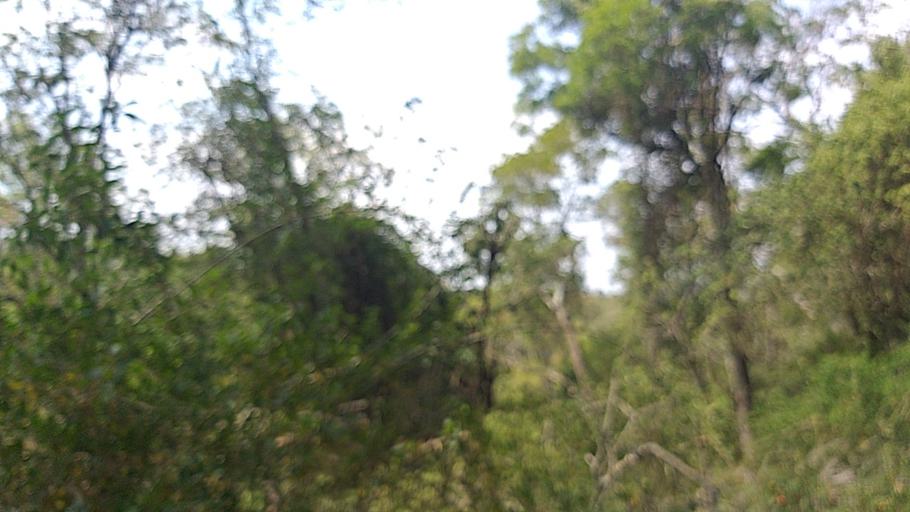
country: AU
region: New South Wales
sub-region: Wollongong
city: Mount Ousley
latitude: -34.4051
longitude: 150.8685
